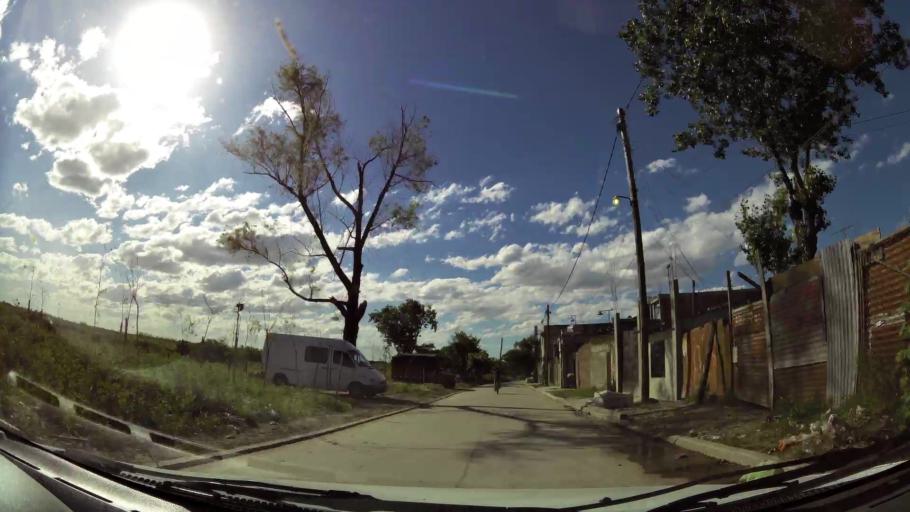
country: AR
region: Buenos Aires
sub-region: Partido de General San Martin
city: General San Martin
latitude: -34.5246
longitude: -58.5832
